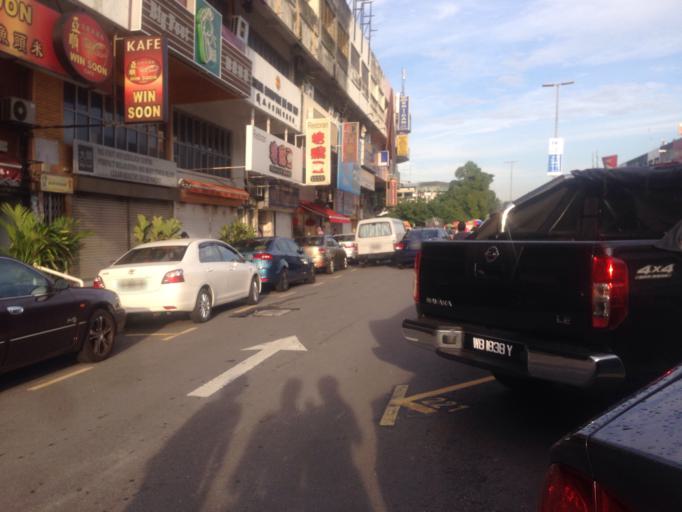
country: MY
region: Selangor
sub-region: Petaling
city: Petaling Jaya
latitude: 3.1190
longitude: 101.6227
